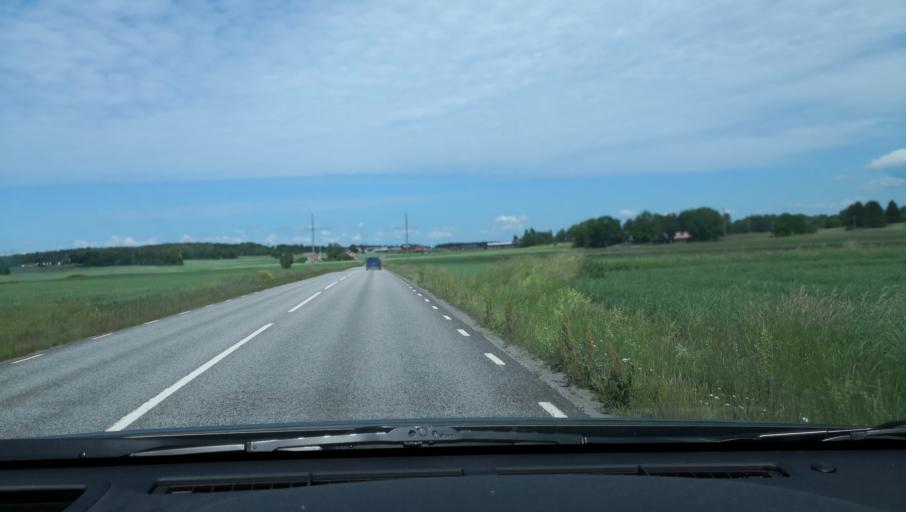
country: SE
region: Stockholm
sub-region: Sigtuna Kommun
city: Sigtuna
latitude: 59.6673
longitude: 17.6931
